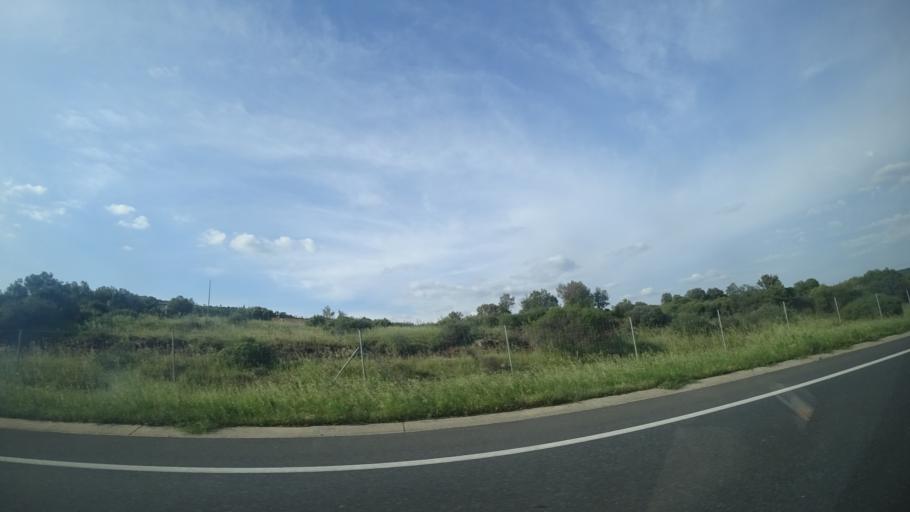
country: FR
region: Languedoc-Roussillon
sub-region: Departement de l'Herault
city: Lodeve
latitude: 43.6852
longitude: 3.3662
